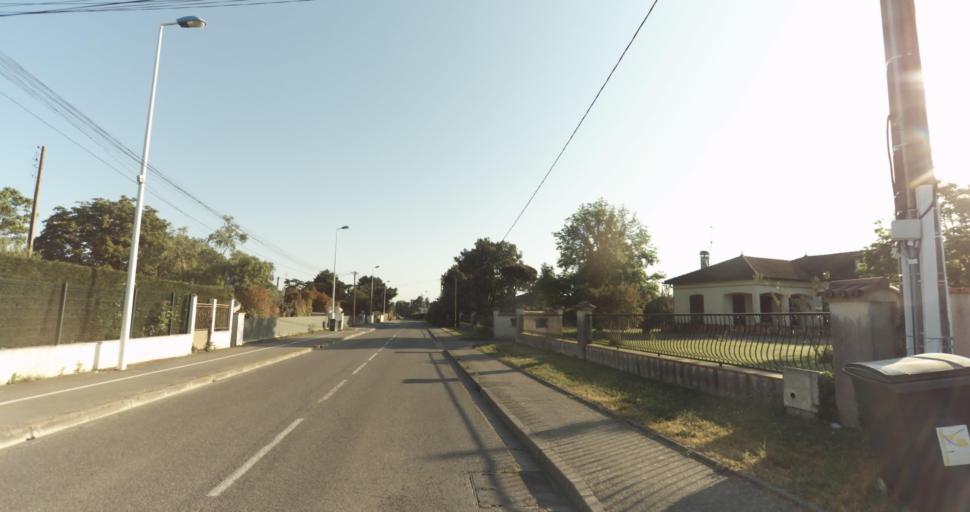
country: FR
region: Midi-Pyrenees
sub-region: Departement de la Haute-Garonne
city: Leguevin
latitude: 43.6046
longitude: 1.2336
